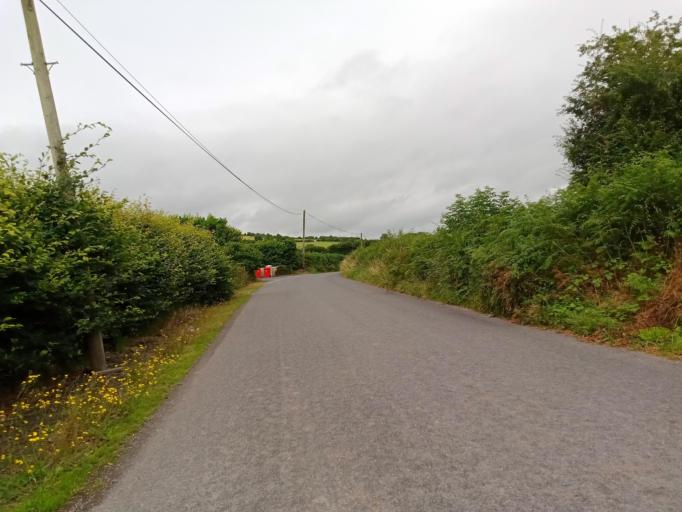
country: IE
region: Leinster
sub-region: Kilkenny
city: Ballyragget
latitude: 52.8120
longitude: -7.4392
